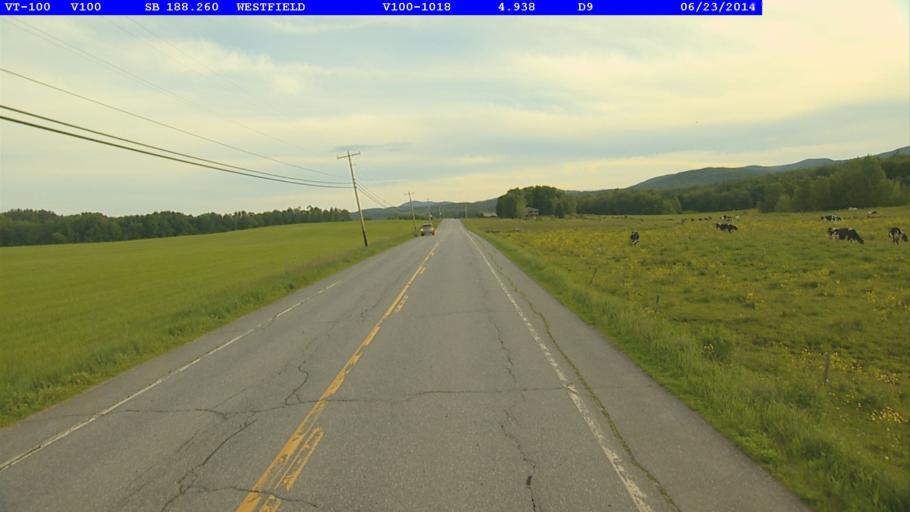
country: US
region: Vermont
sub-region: Orleans County
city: Newport
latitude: 44.8993
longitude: -72.4104
